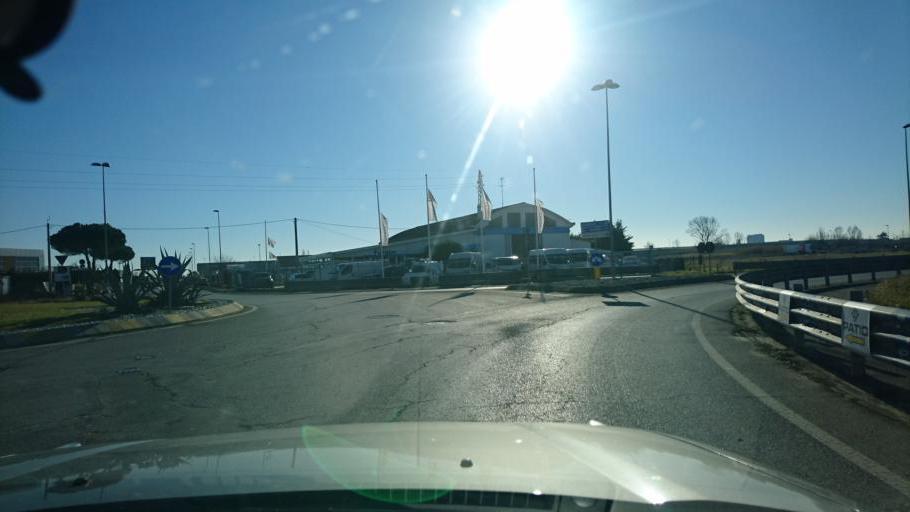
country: IT
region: Veneto
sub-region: Provincia di Rovigo
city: Porto Viro
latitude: 45.0319
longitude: 12.2340
